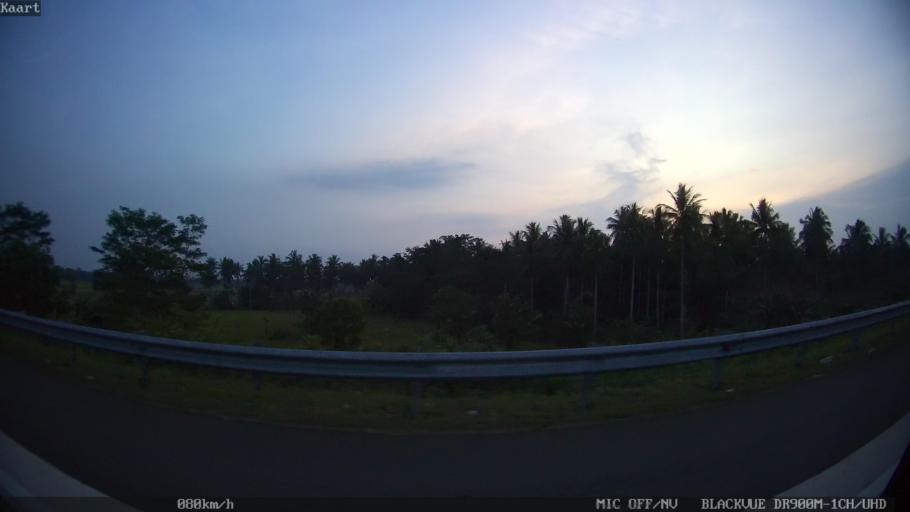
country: ID
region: Lampung
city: Kalianda
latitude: -5.6612
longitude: 105.5912
